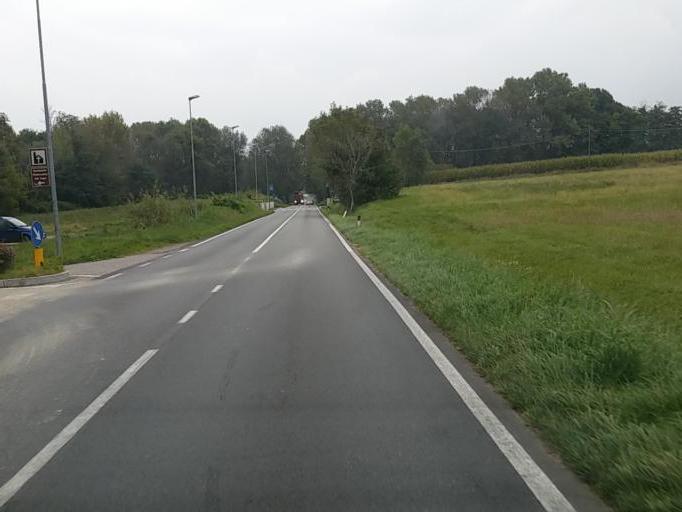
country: IT
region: Lombardy
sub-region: Provincia di Varese
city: Galliate Lombardo
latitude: 45.7884
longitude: 8.7834
